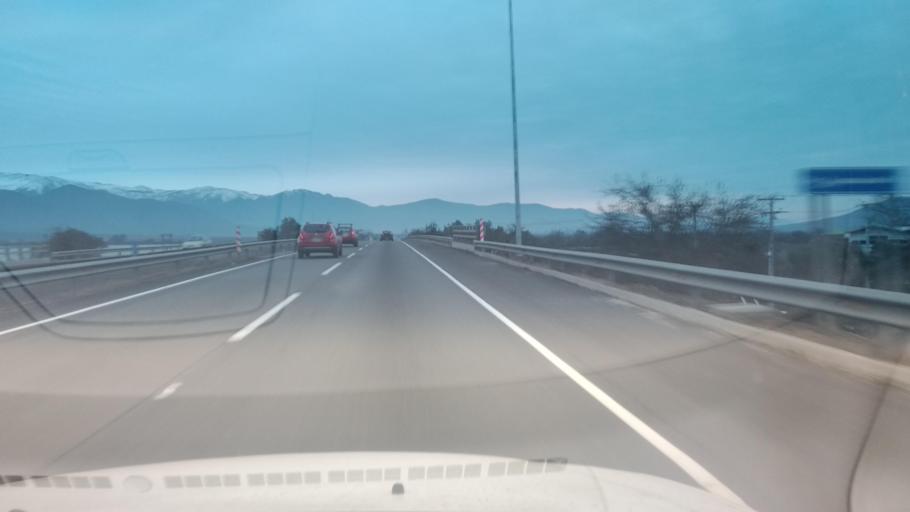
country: CL
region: Santiago Metropolitan
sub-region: Provincia de Chacabuco
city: Chicureo Abajo
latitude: -33.1451
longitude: -70.6590
